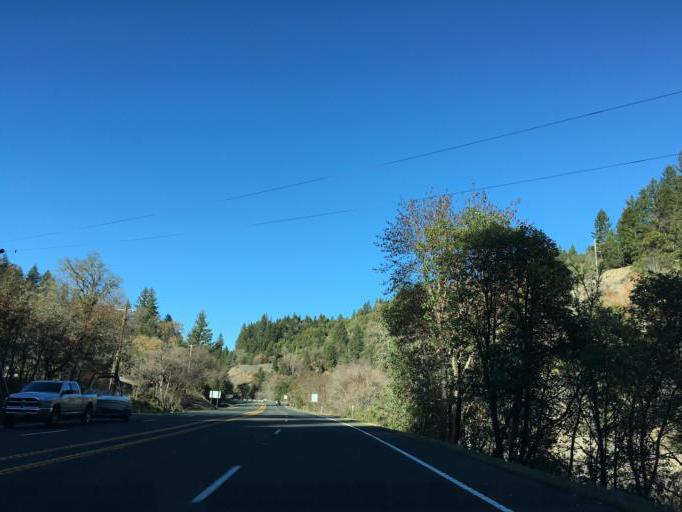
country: US
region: California
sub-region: Mendocino County
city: Brooktrails
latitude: 39.5599
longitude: -123.4328
